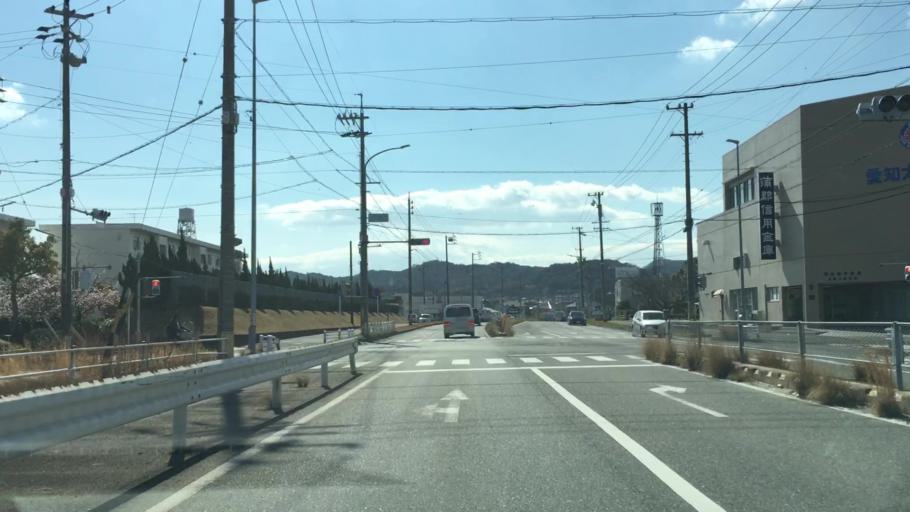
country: JP
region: Aichi
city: Gamagori
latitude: 34.8086
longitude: 137.1918
